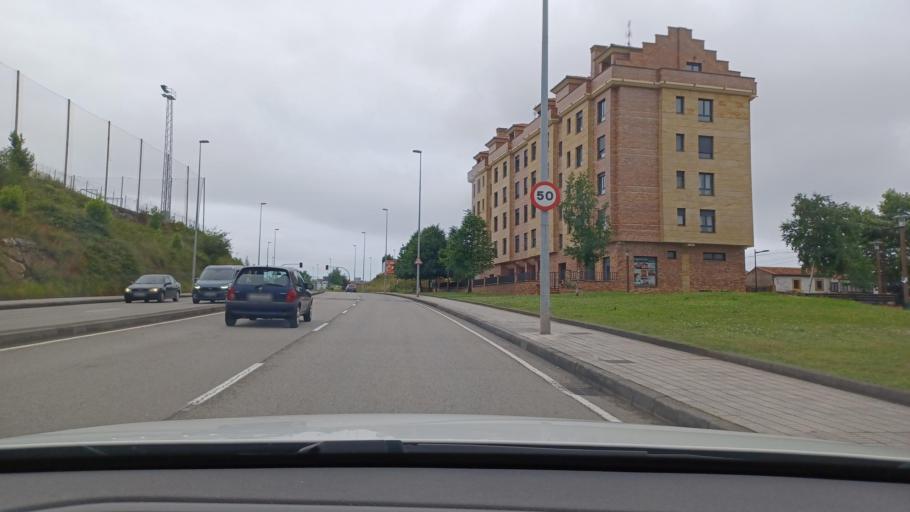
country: ES
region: Asturias
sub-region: Province of Asturias
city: Gijon
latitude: 43.5253
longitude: -5.6554
